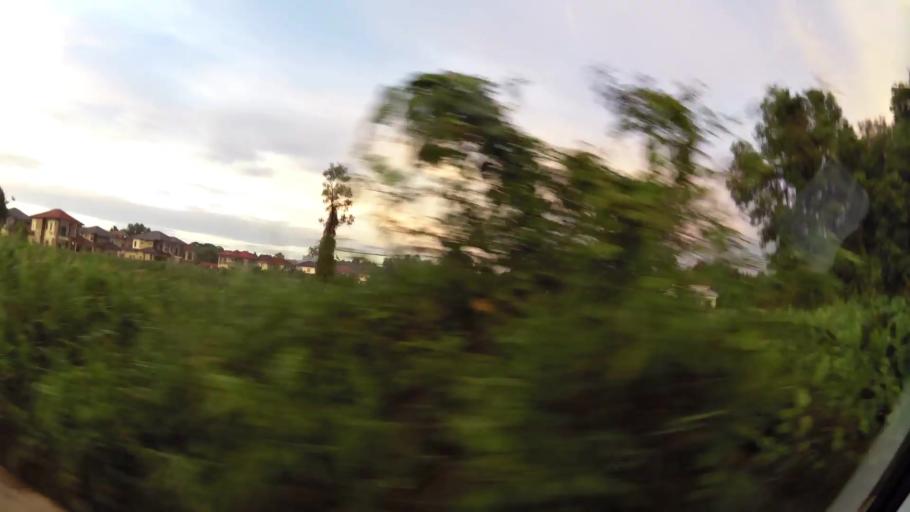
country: BN
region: Brunei and Muara
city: Bandar Seri Begawan
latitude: 4.9996
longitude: 114.9969
